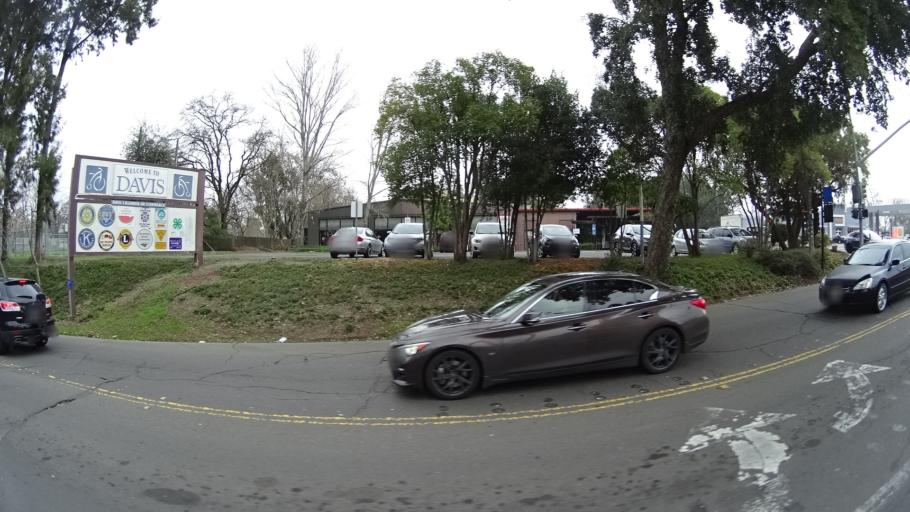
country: US
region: California
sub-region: Yolo County
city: Davis
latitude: 38.5410
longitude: -121.7389
